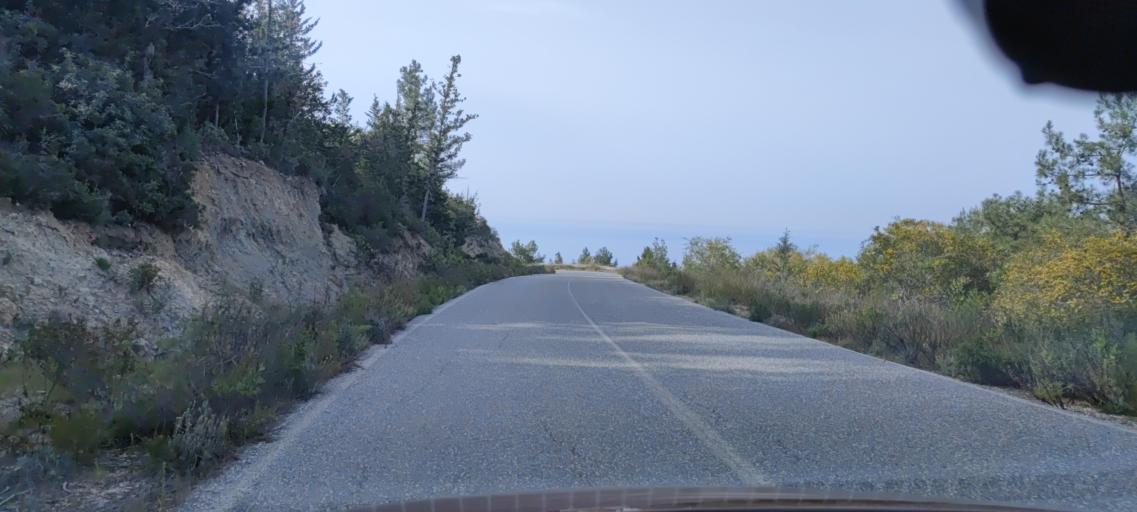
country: CY
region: Ammochostos
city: Trikomo
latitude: 35.3880
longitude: 33.8955
